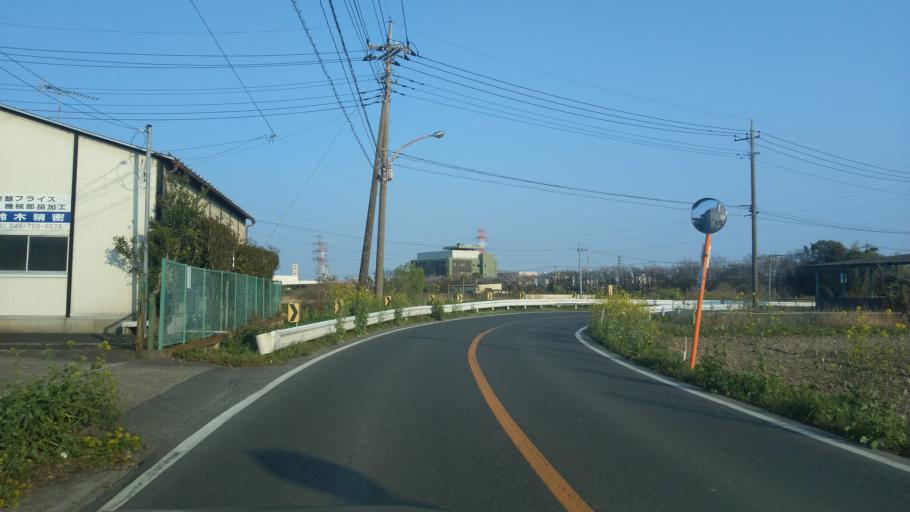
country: JP
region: Saitama
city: Shobu
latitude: 36.0283
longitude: 139.5872
